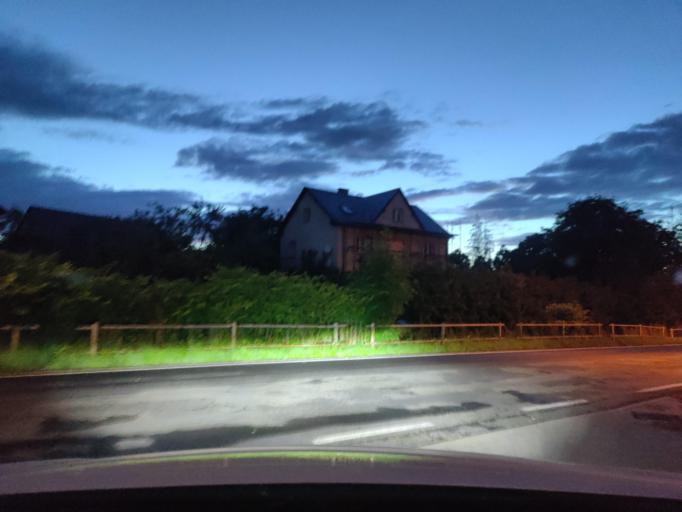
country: CZ
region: Olomoucky
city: Zlate Hory
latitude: 50.2552
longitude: 17.3998
